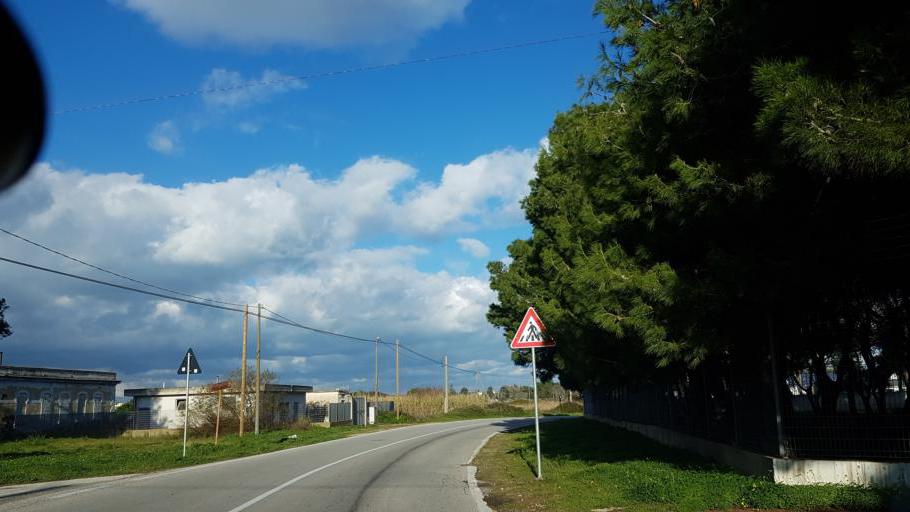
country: IT
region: Apulia
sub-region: Provincia di Brindisi
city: Materdomini
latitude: 40.6648
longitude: 17.9500
